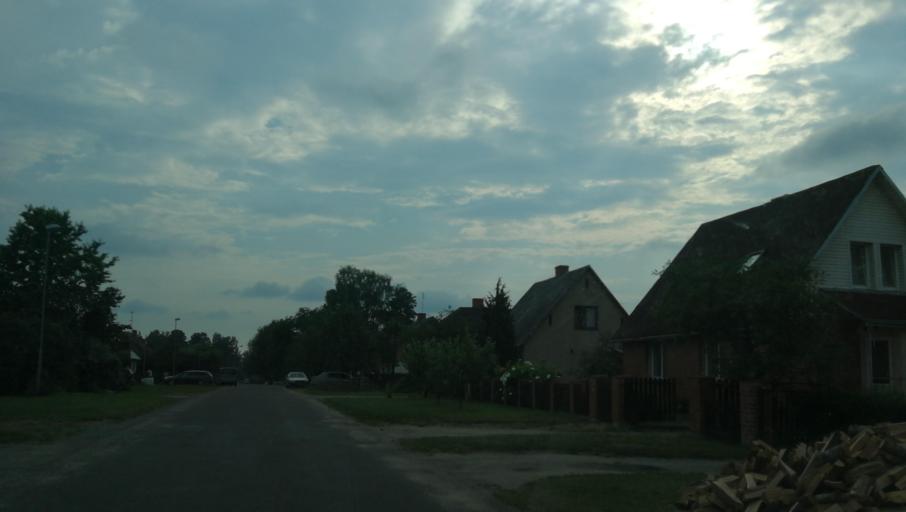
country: LV
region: Cesu Rajons
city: Cesis
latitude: 57.3206
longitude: 25.2721
